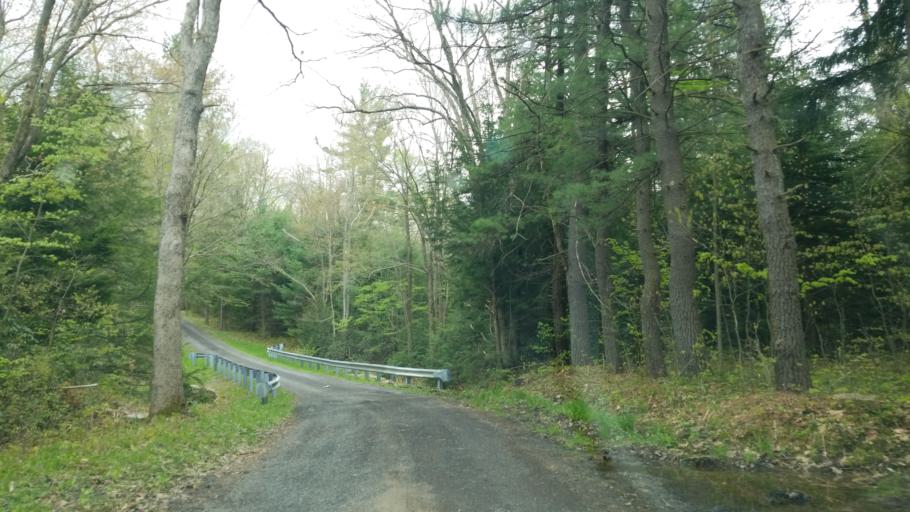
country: US
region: Pennsylvania
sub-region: Clearfield County
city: Shiloh
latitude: 41.2080
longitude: -78.1511
